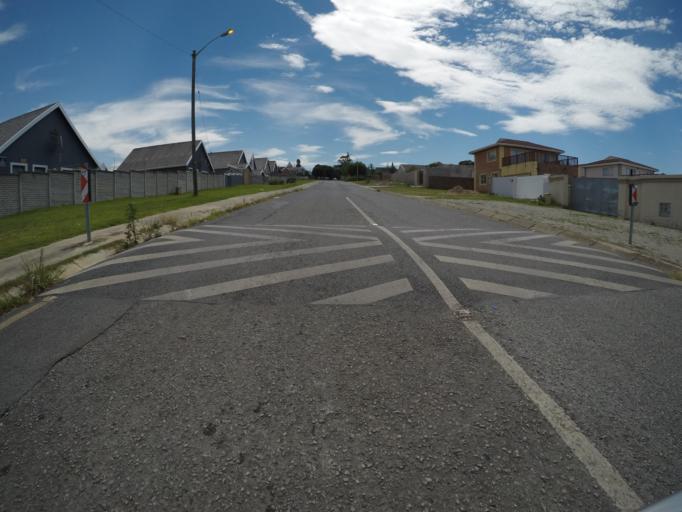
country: ZA
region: Eastern Cape
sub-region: Buffalo City Metropolitan Municipality
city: East London
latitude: -33.0400
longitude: 27.8620
